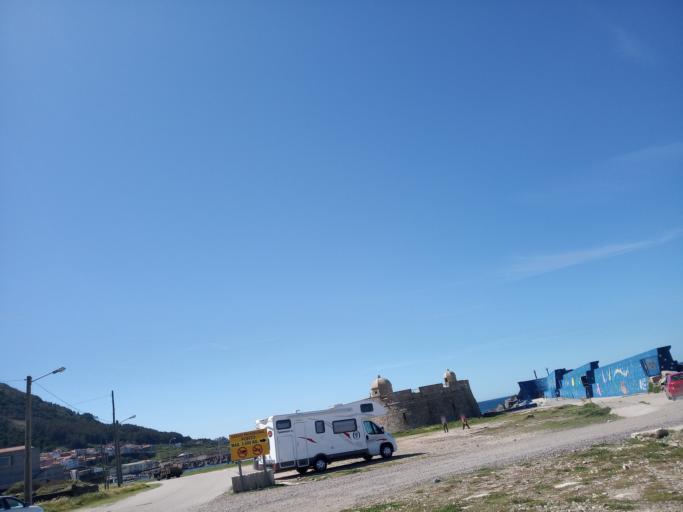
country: ES
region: Galicia
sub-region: Provincia de Pontevedra
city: A Guarda
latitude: 41.9031
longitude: -8.8800
